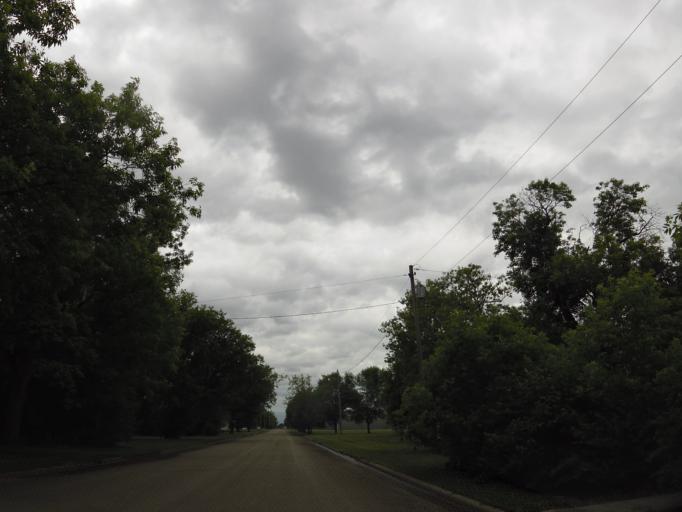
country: US
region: North Dakota
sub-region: Walsh County
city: Grafton
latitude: 48.6161
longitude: -97.4437
